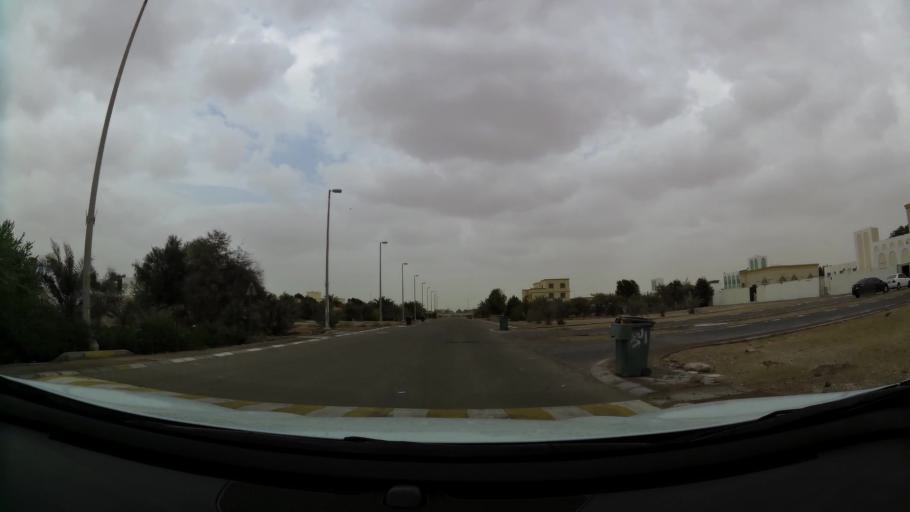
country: AE
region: Abu Dhabi
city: Abu Dhabi
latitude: 24.3315
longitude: 54.6432
